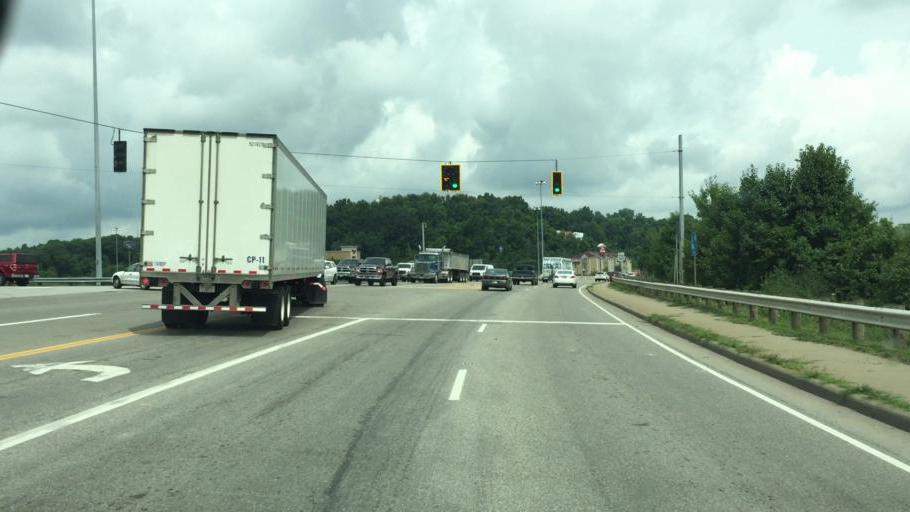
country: US
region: Ohio
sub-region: Guernsey County
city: Cambridge
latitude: 39.9975
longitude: -81.5781
